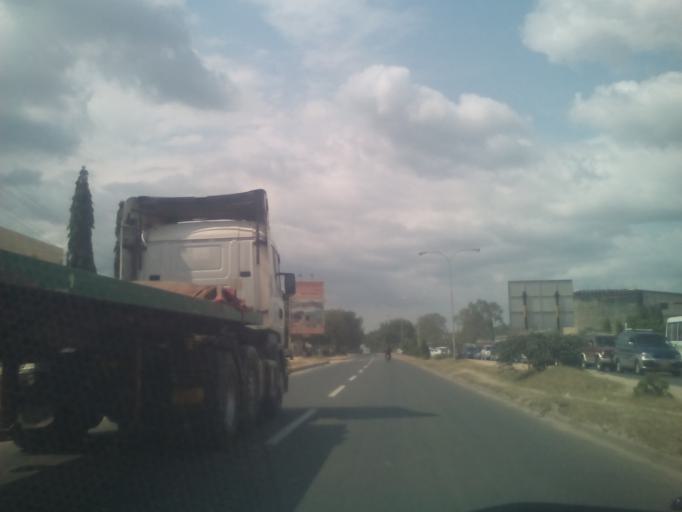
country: TZ
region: Dar es Salaam
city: Dar es Salaam
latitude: -6.8435
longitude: 39.2466
